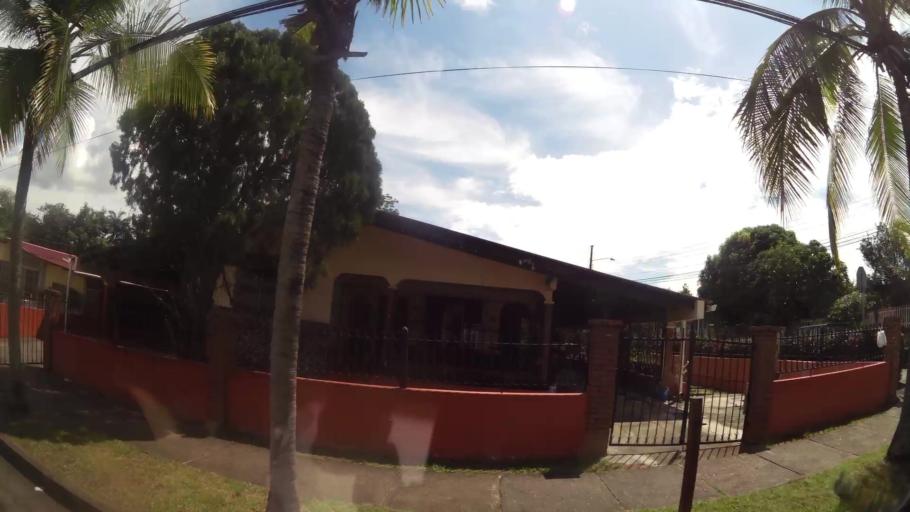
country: PA
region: Panama
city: Vista Alegre
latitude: 8.9216
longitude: -79.6955
